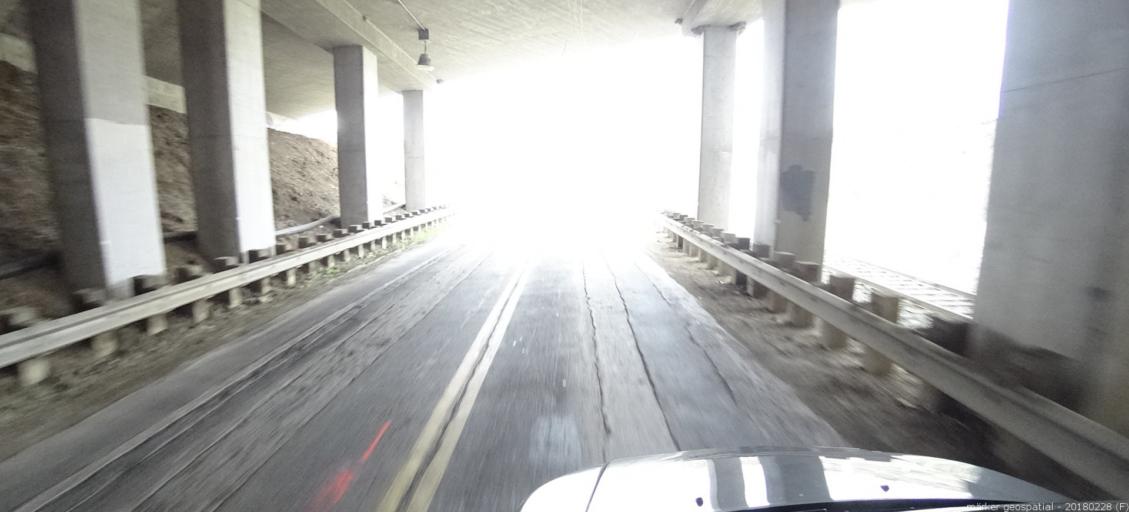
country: US
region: California
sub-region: El Dorado County
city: El Dorado Hills
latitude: 38.6435
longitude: -121.1102
